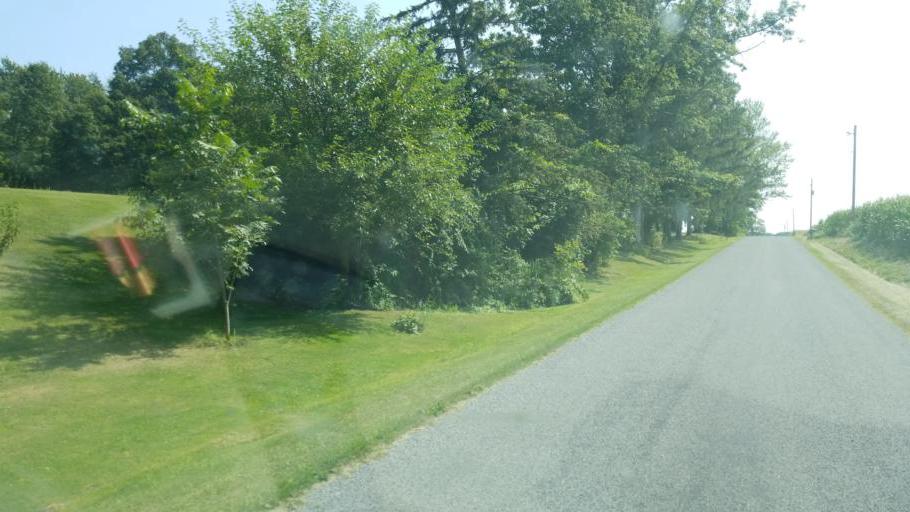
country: US
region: Ohio
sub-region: Crawford County
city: Crestline
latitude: 40.9018
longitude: -82.7981
